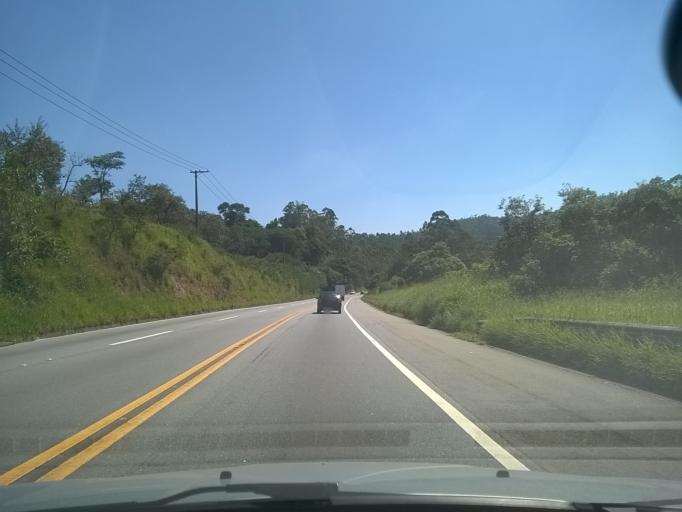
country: BR
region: Sao Paulo
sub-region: Francisco Morato
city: Francisco Morato
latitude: -23.2910
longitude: -46.7884
